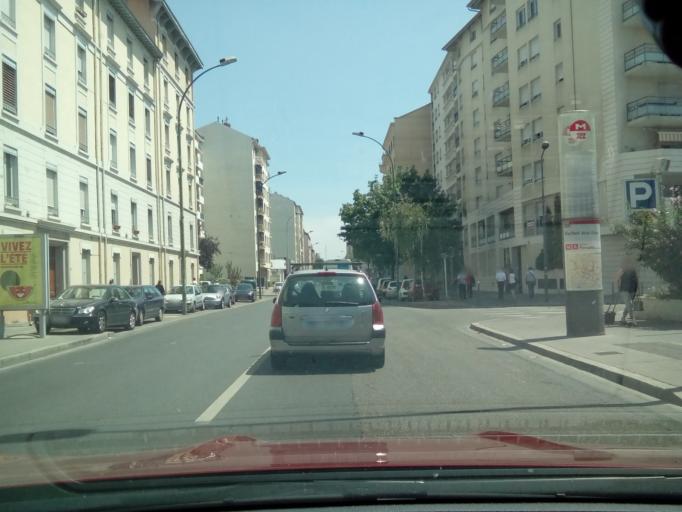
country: FR
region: Rhone-Alpes
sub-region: Departement du Rhone
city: Villeurbanne
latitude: 45.7675
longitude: 4.8903
